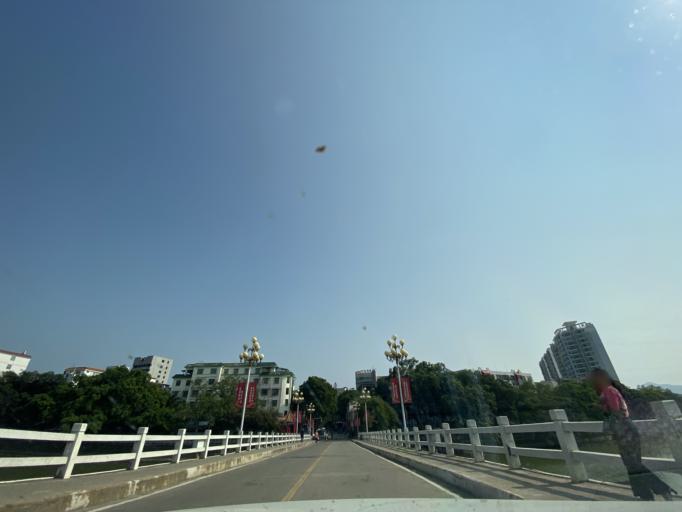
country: CN
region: Hainan
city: Chongshan
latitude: 18.7816
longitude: 109.5114
